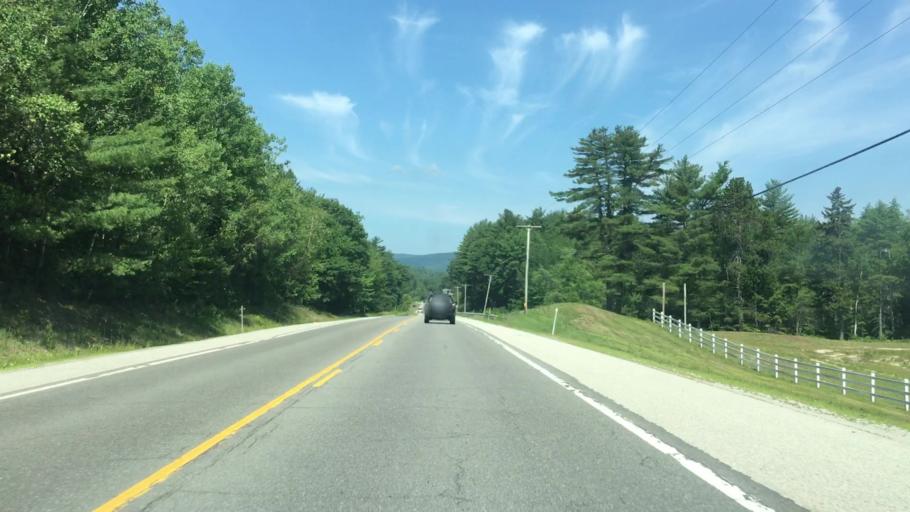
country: US
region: New Hampshire
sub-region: Merrimack County
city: Sutton
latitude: 43.2562
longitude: -71.9340
